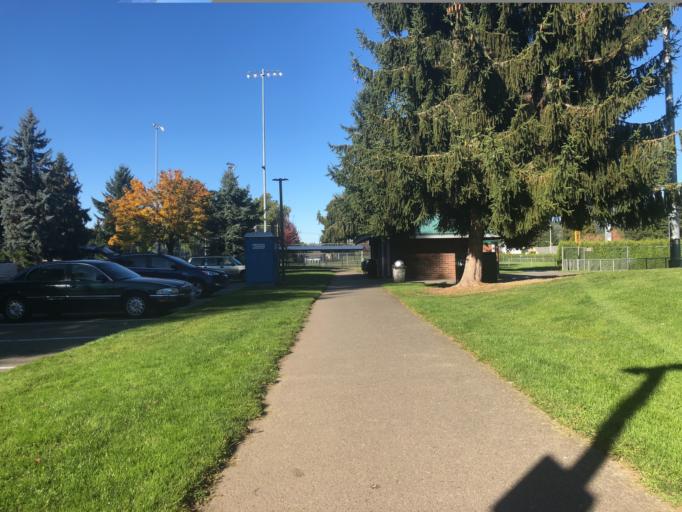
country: US
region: Washington
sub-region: King County
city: Auburn
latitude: 47.3317
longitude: -122.2147
